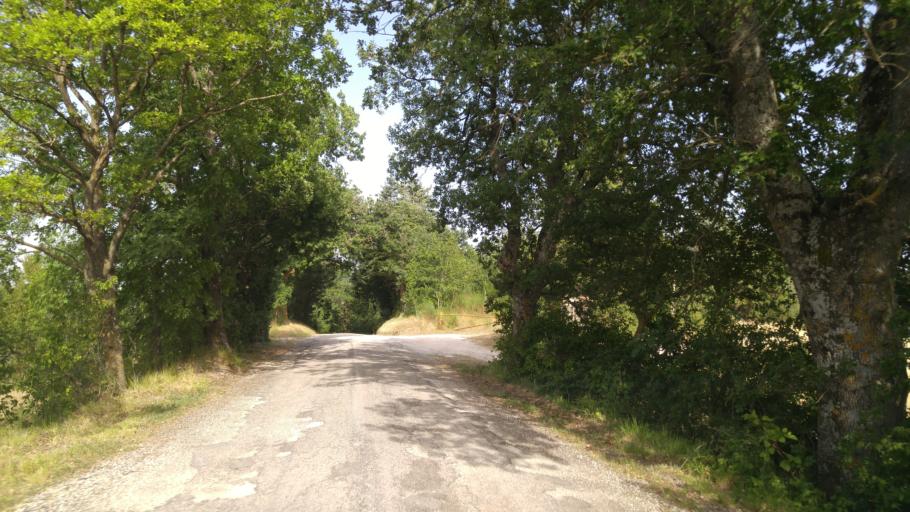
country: IT
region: The Marches
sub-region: Provincia di Pesaro e Urbino
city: Canavaccio
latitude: 43.6676
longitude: 12.7452
